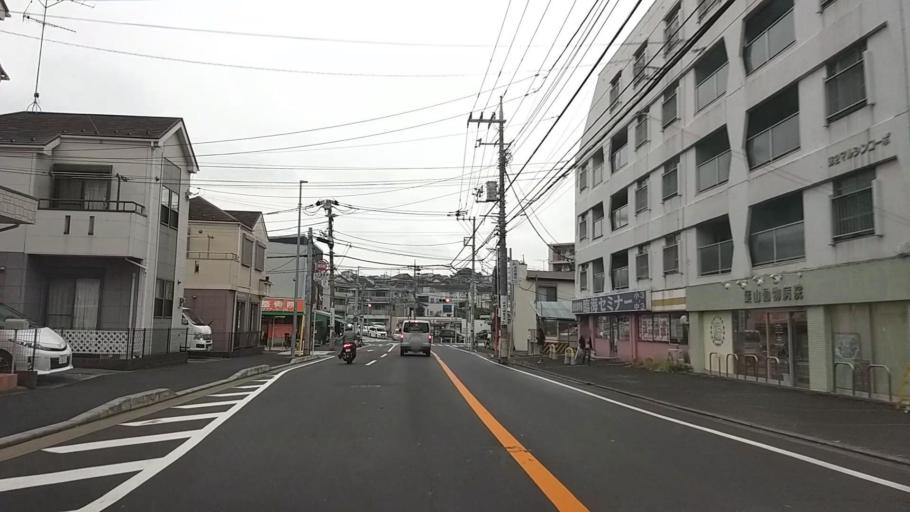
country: JP
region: Kanagawa
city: Yokohama
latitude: 35.4126
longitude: 139.6089
